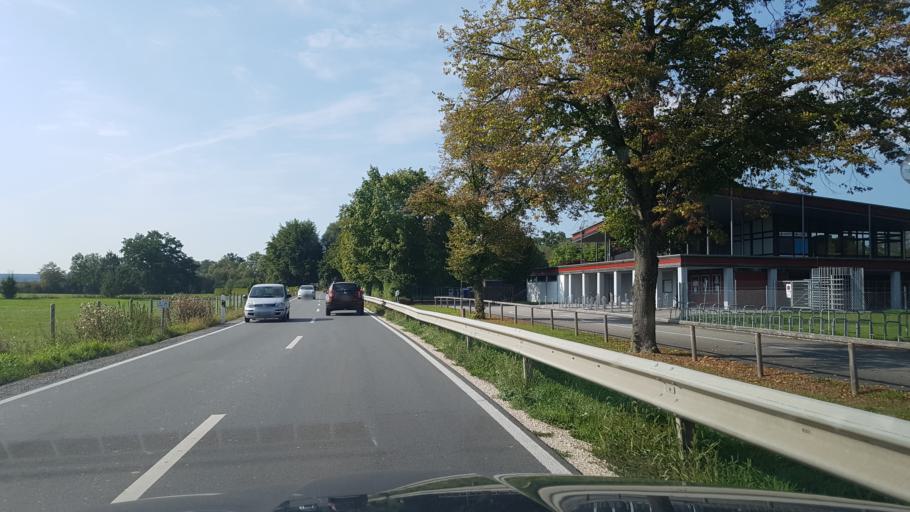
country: DE
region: Bavaria
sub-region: Upper Bavaria
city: Ainring
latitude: 47.8458
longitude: 12.9472
